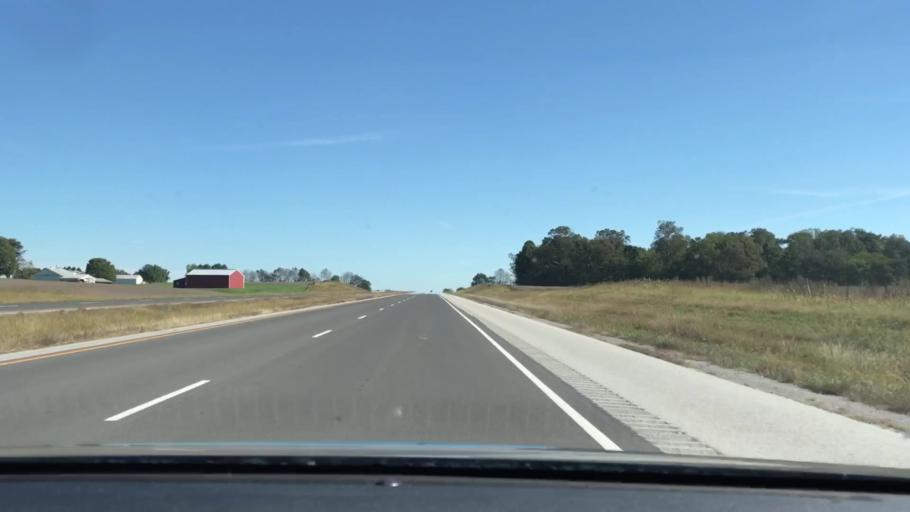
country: US
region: Kentucky
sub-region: Logan County
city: Russellville
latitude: 36.8172
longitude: -87.0041
